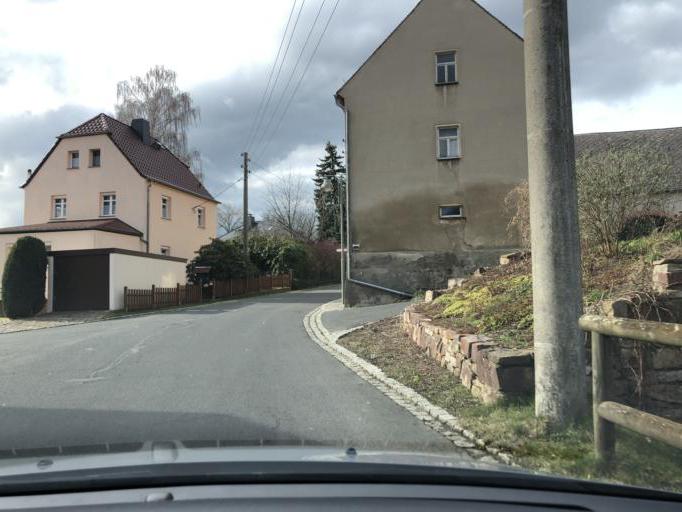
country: DE
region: Saxony
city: Ostrau
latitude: 51.2068
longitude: 12.8842
